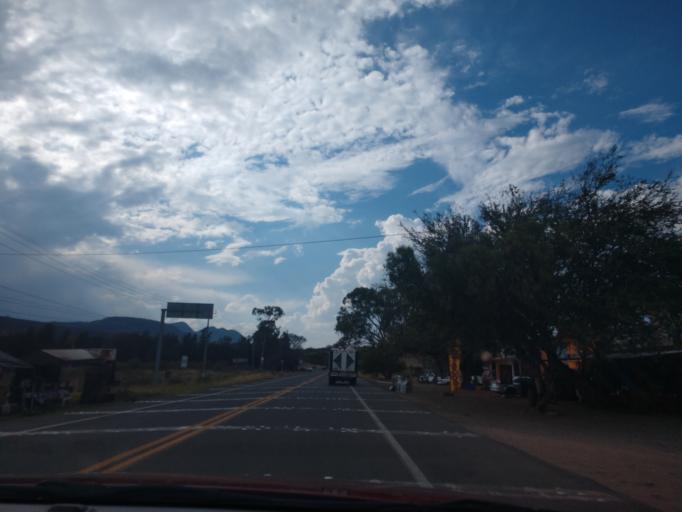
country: MX
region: Jalisco
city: Chapala
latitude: 20.1534
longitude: -103.1867
